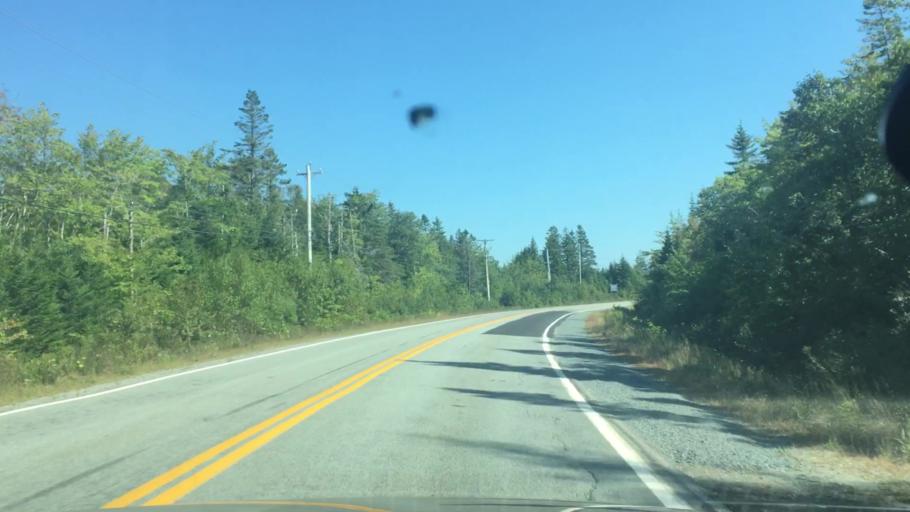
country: CA
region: Nova Scotia
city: New Glasgow
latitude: 44.9084
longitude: -62.5550
